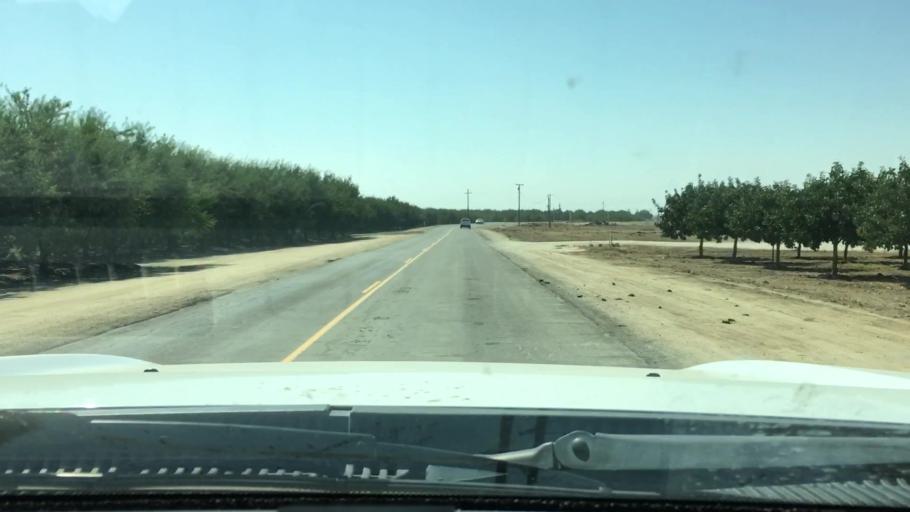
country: US
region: California
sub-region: Kern County
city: Shafter
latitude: 35.5534
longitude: -119.2769
